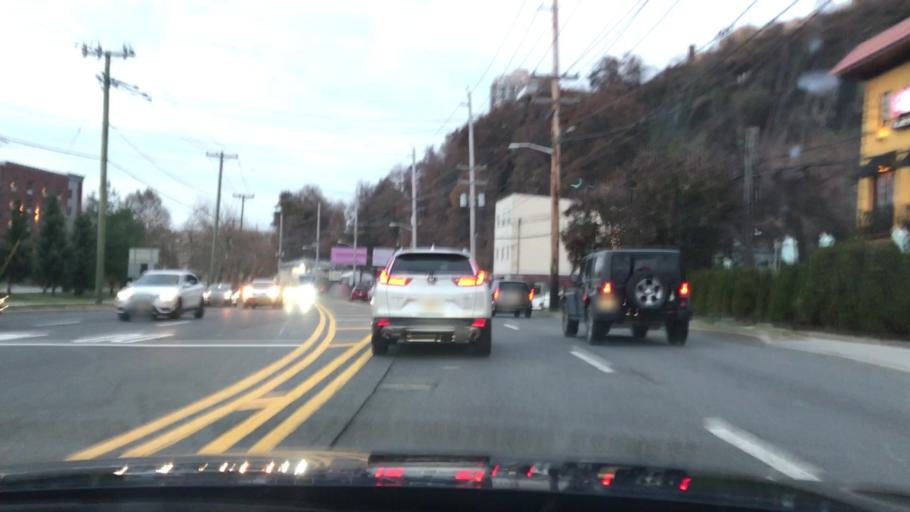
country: US
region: New Jersey
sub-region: Bergen County
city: Fairview
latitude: 40.8041
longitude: -73.9934
